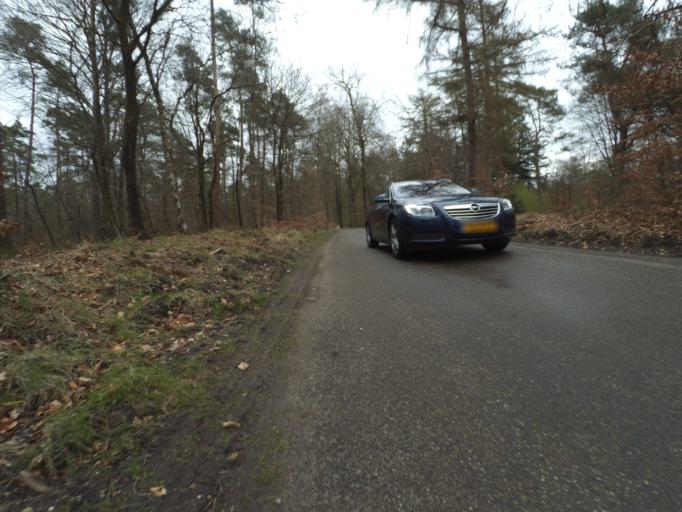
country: NL
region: Gelderland
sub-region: Gemeente Apeldoorn
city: Loenen
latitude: 52.1060
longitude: 6.0030
